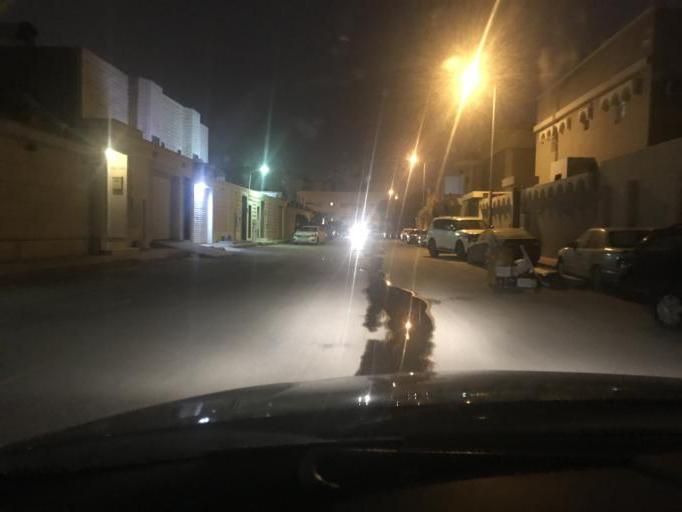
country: SA
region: Ar Riyad
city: Riyadh
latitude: 24.7495
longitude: 46.7753
